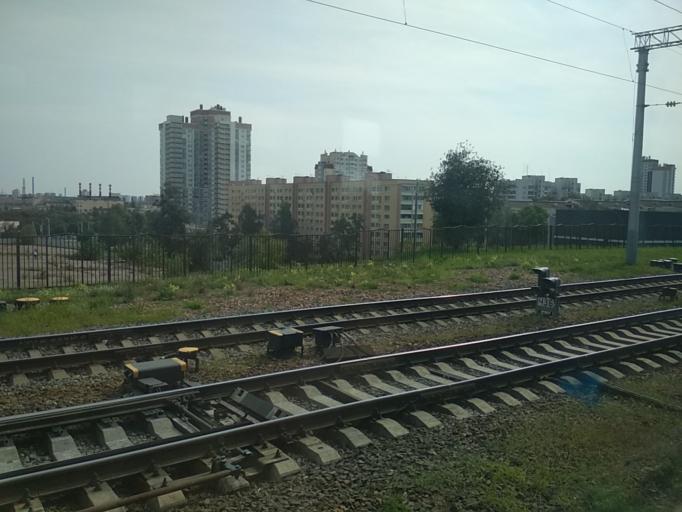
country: BY
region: Minsk
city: Minsk
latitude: 53.8847
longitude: 27.5633
